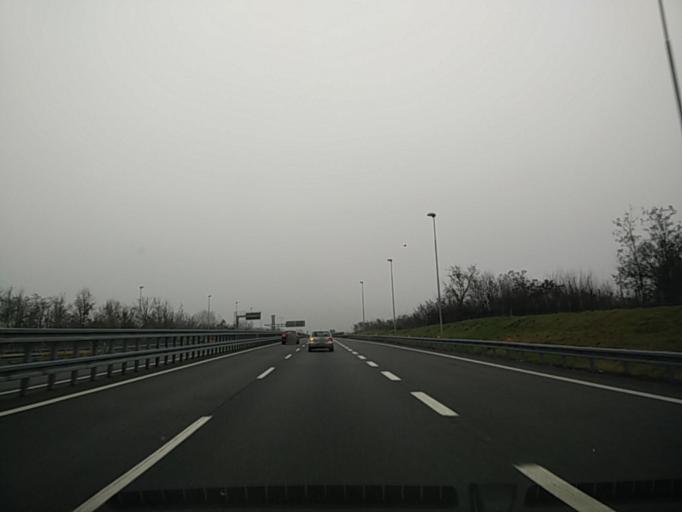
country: IT
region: Piedmont
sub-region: Provincia di Alessandria
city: Quattordio
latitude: 44.9097
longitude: 8.4084
